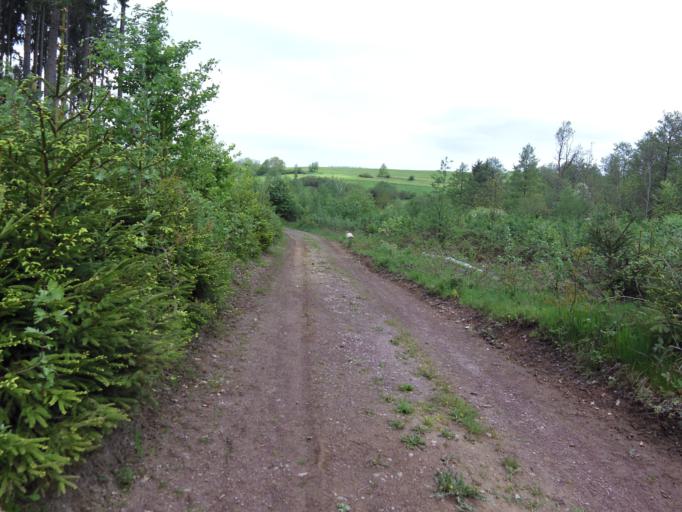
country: DE
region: Thuringia
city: Herrenhof
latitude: 50.8193
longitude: 10.6764
